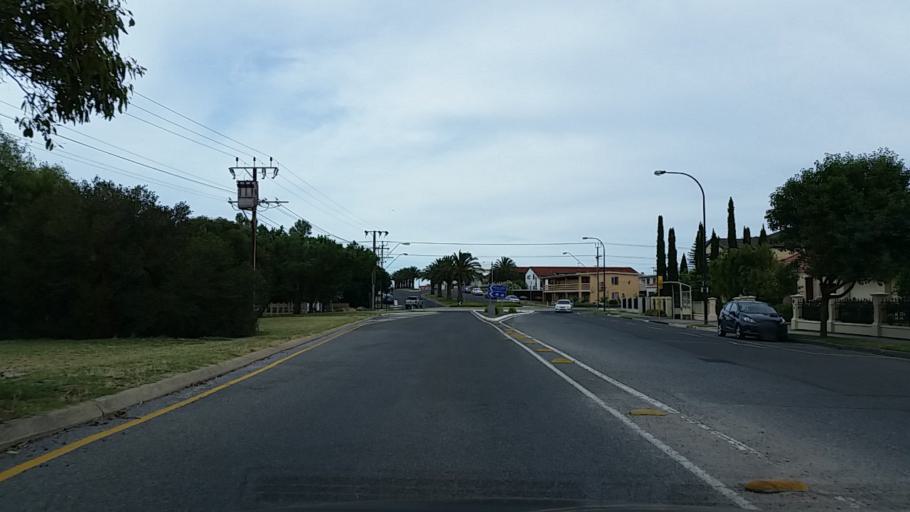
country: AU
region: South Australia
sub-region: Charles Sturt
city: Henley Beach
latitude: -34.9453
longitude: 138.5056
